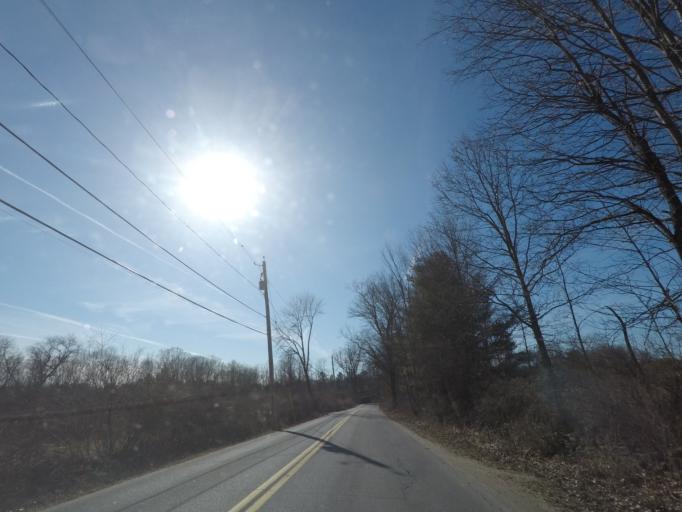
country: US
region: New York
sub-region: Saratoga County
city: Milton
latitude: 43.0726
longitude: -73.8350
